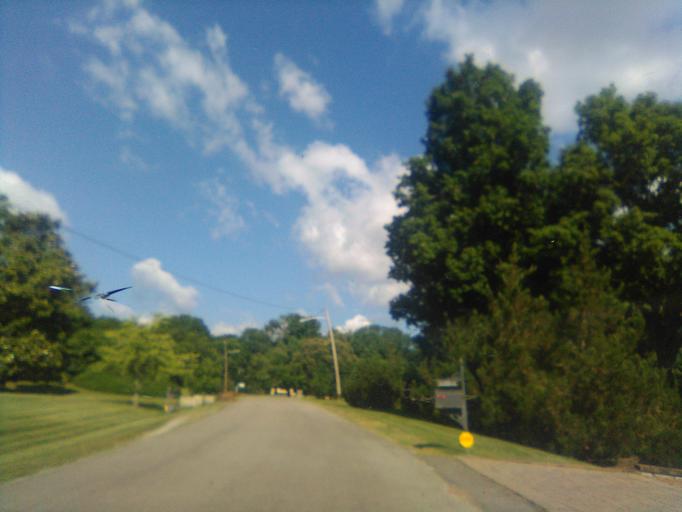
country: US
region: Tennessee
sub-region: Davidson County
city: Belle Meade
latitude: 36.1142
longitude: -86.8668
